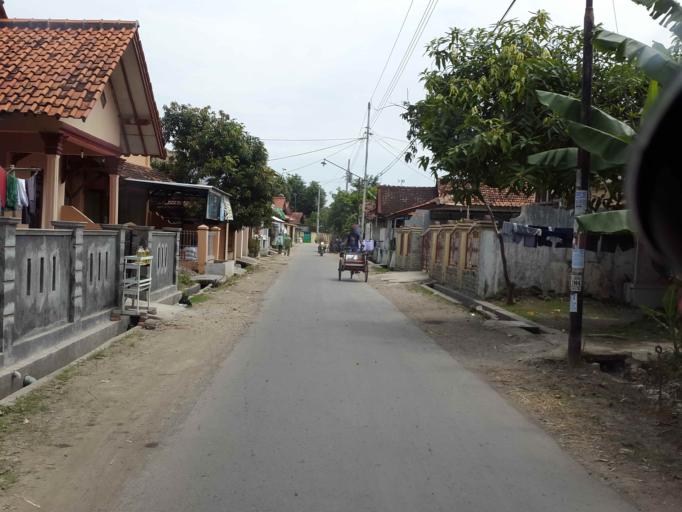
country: ID
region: Central Java
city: Petarukan
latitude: -6.8917
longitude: 109.4004
